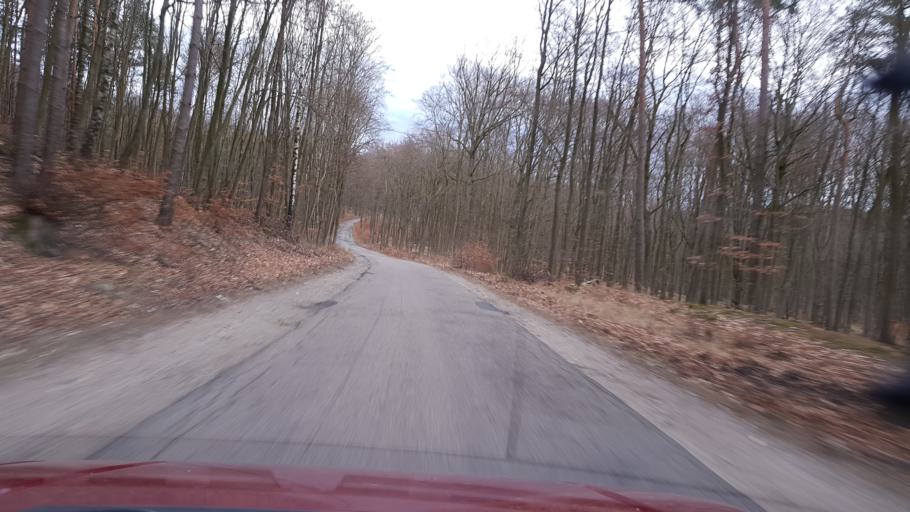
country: PL
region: West Pomeranian Voivodeship
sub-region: Szczecin
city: Szczecin
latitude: 53.3453
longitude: 14.6174
